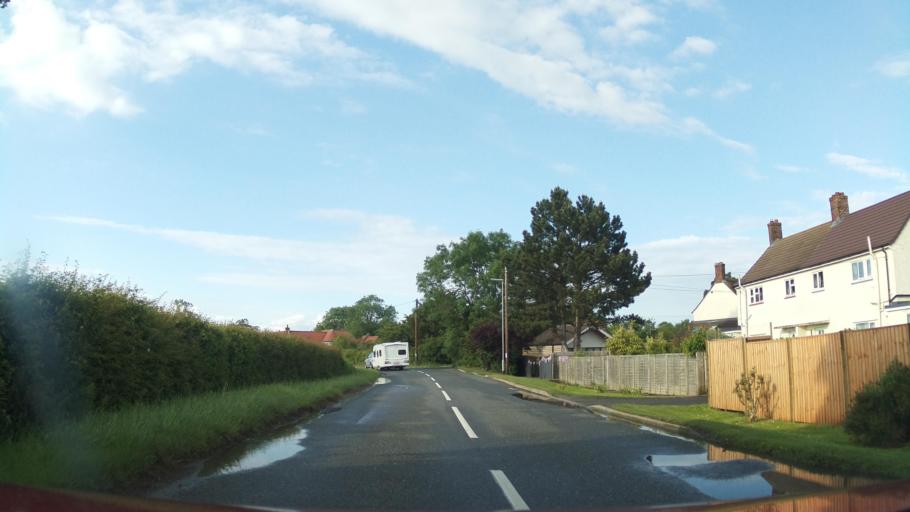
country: GB
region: England
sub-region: Lincolnshire
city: Great Gonerby
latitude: 53.0215
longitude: -0.6570
